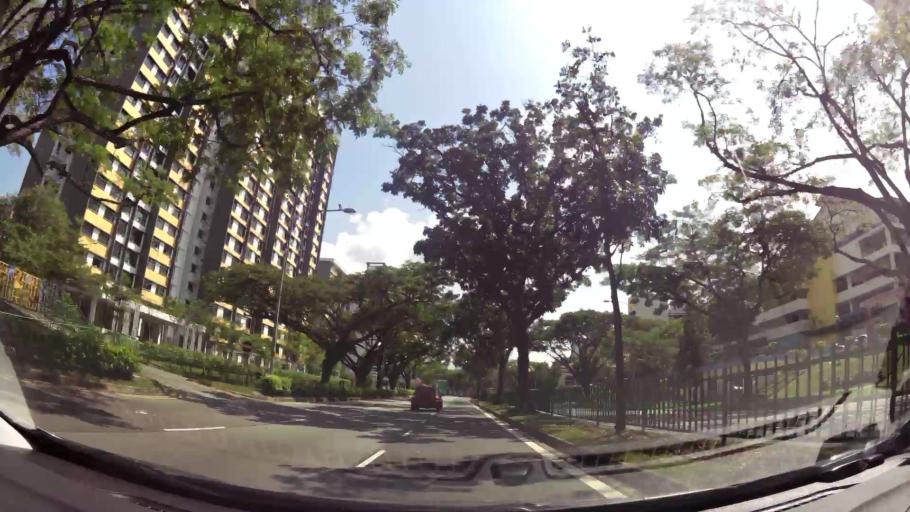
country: SG
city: Singapore
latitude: 1.3773
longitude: 103.8423
